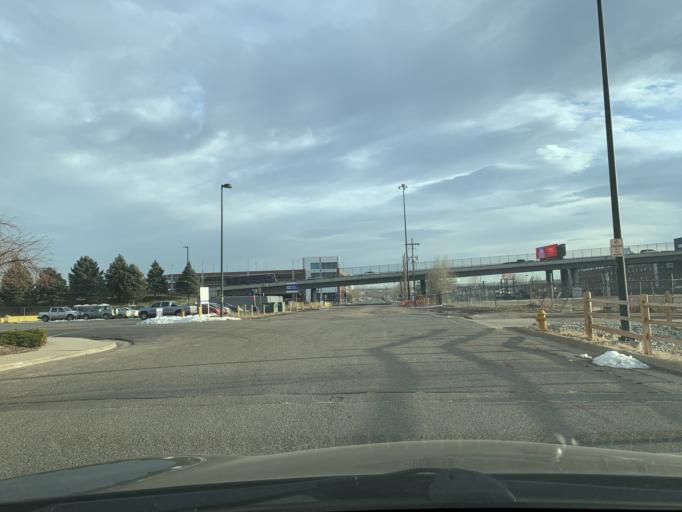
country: US
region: Colorado
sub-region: Denver County
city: Denver
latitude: 39.7449
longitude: -105.0125
